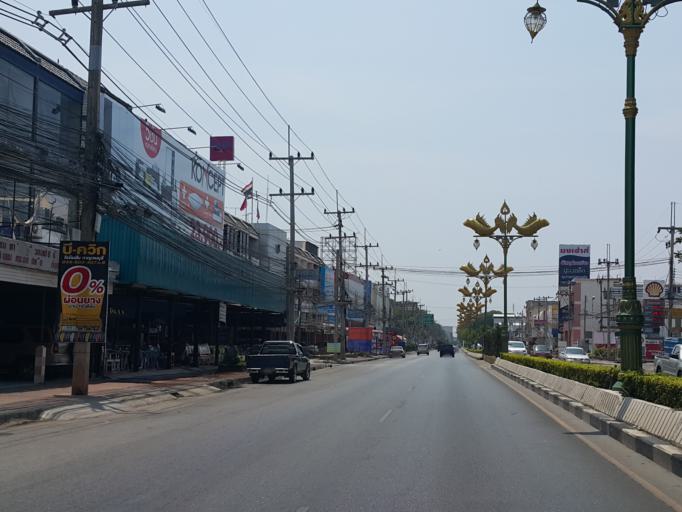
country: TH
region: Kanchanaburi
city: Kanchanaburi
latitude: 14.0358
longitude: 99.5217
